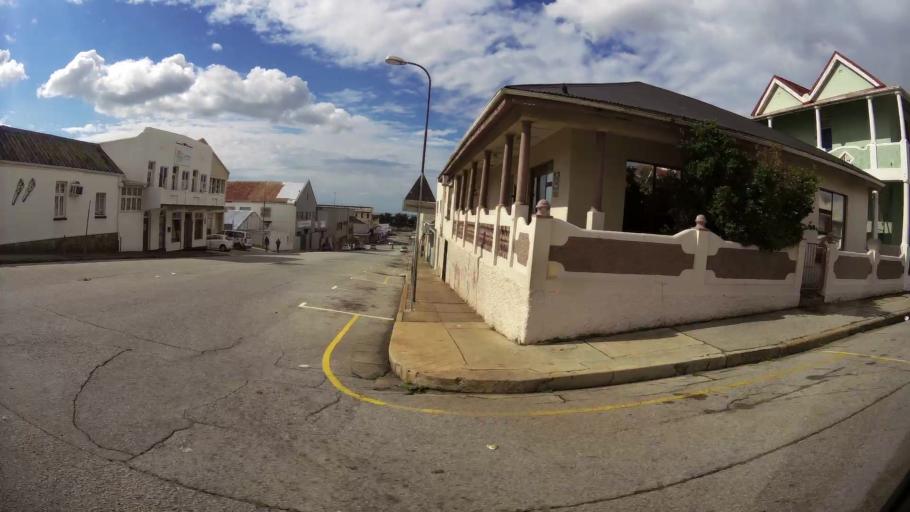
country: ZA
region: Eastern Cape
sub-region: Nelson Mandela Bay Metropolitan Municipality
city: Port Elizabeth
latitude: -33.9499
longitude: 25.6061
